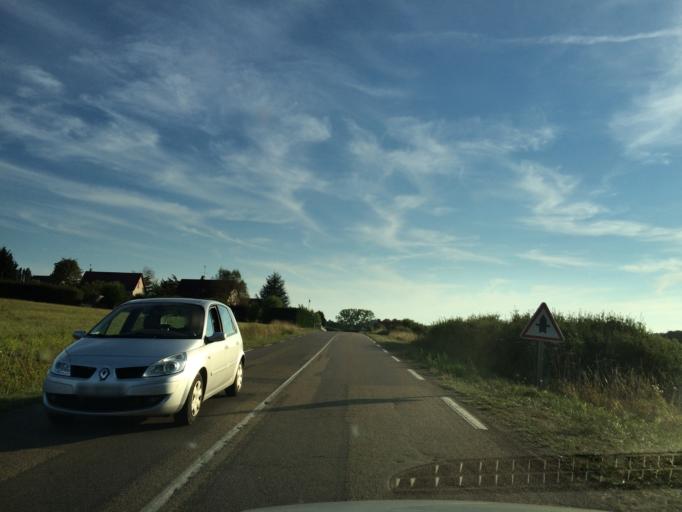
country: FR
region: Bourgogne
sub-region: Departement de l'Yonne
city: Saint-Georges-sur-Baulche
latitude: 47.8319
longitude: 3.5454
